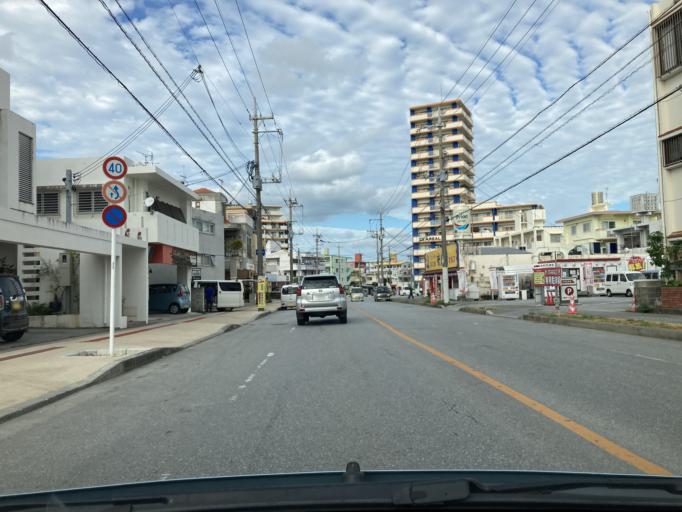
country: JP
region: Okinawa
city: Okinawa
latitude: 26.3403
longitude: 127.8220
